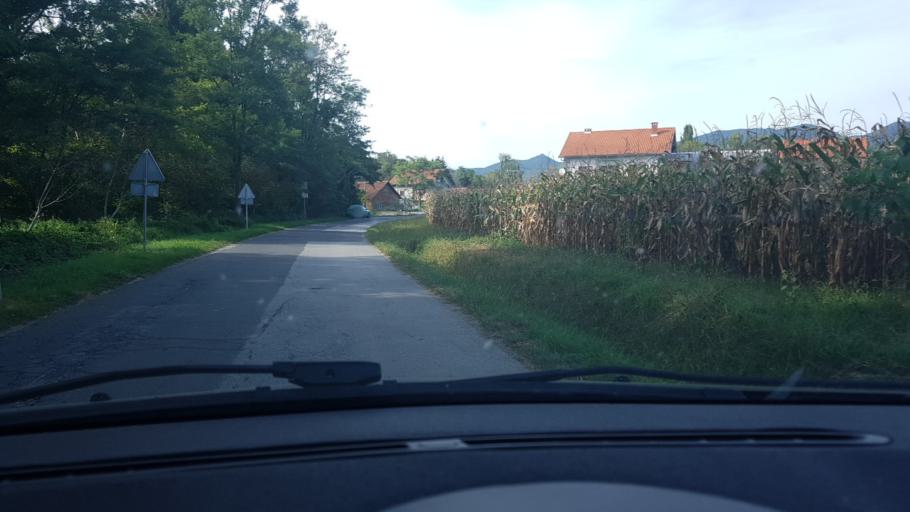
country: HR
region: Krapinsko-Zagorska
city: Zlatar
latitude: 46.1175
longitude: 16.1121
